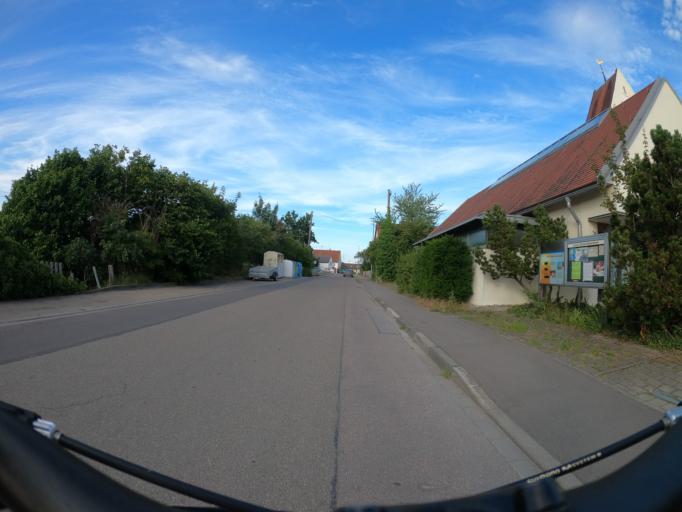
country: DE
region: Bavaria
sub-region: Swabia
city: Nersingen
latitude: 48.4301
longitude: 10.1252
